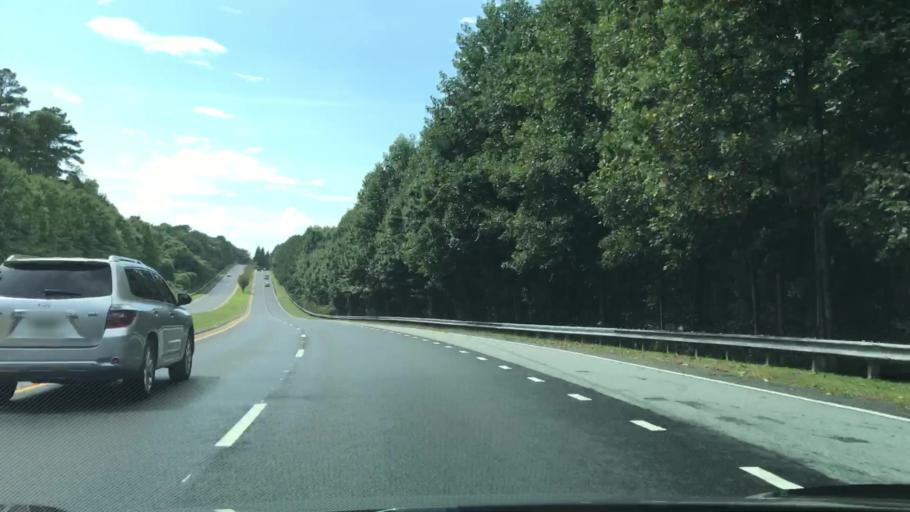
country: US
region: Georgia
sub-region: Gwinnett County
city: Lilburn
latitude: 33.9134
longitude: -84.1059
